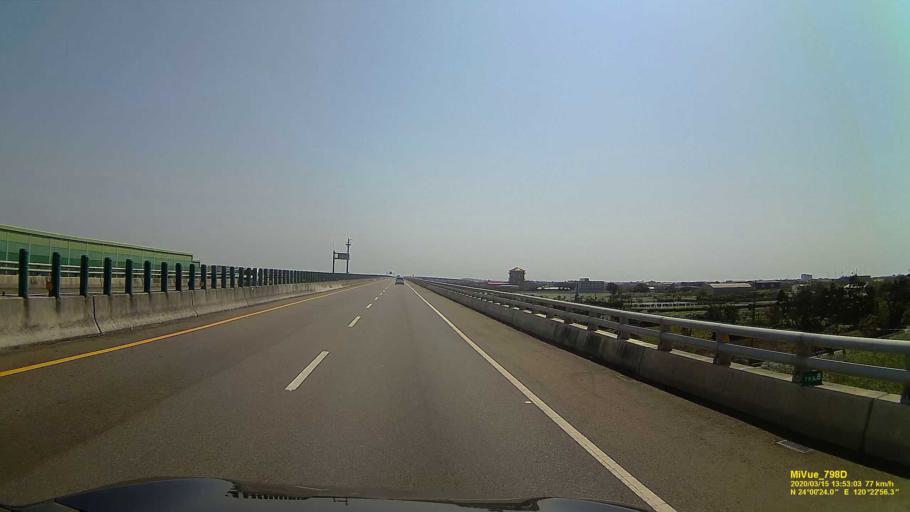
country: TW
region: Taiwan
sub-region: Changhua
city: Chang-hua
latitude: 24.0064
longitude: 120.3822
